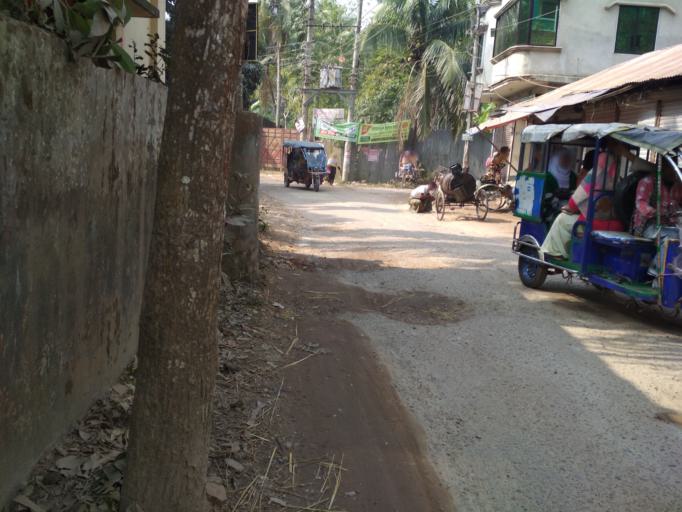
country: BD
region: Chittagong
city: Lakshmipur
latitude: 22.9346
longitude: 90.8243
